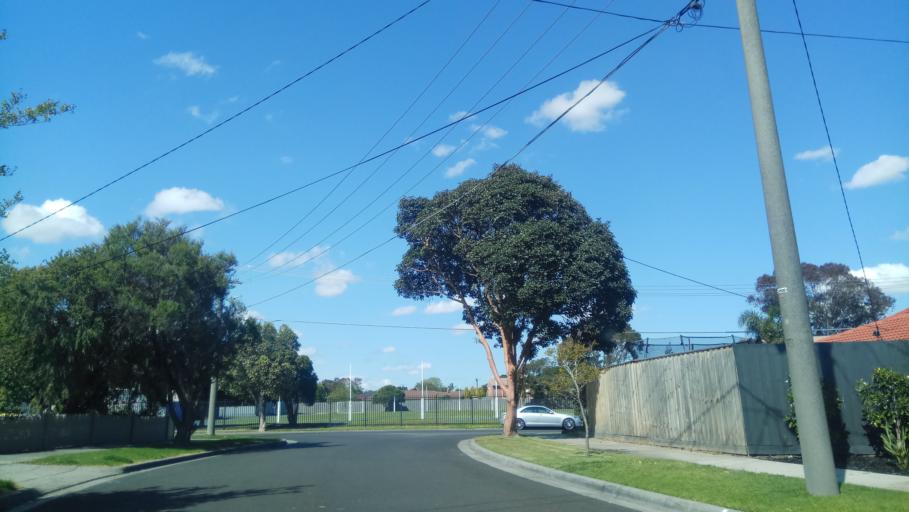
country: AU
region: Victoria
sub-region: Kingston
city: Dingley Village
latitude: -37.9836
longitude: 145.1227
